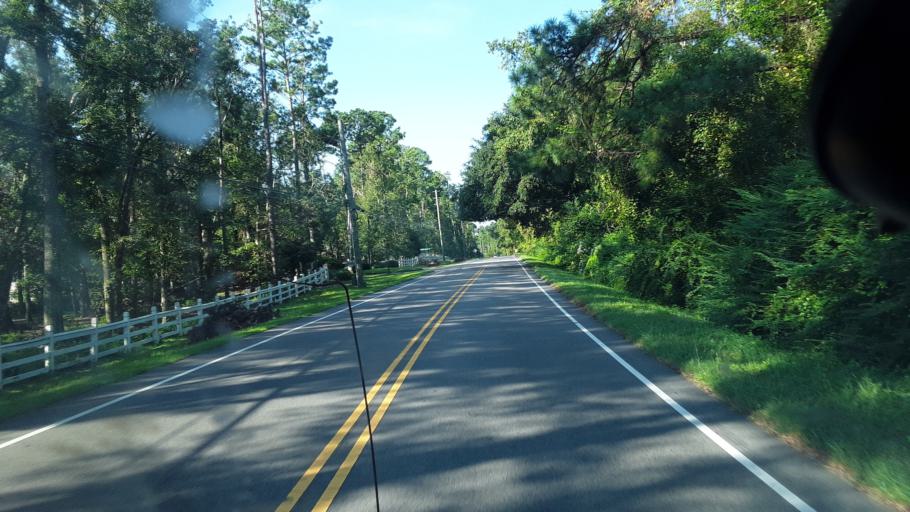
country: US
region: North Carolina
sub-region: Brunswick County
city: Belville
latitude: 34.1978
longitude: -77.9815
